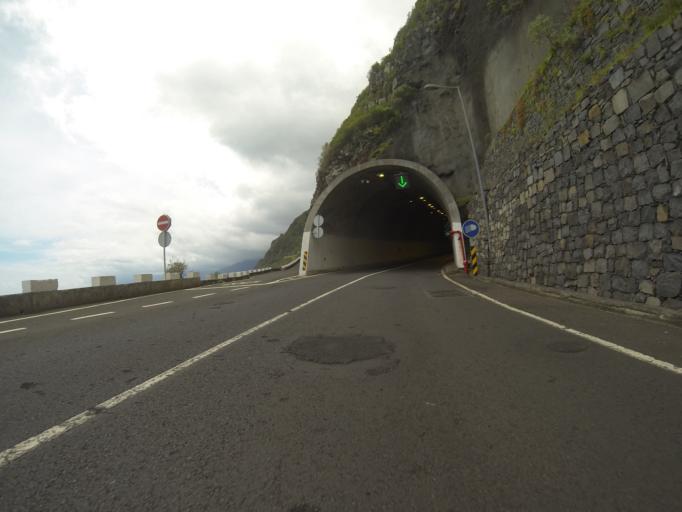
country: PT
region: Madeira
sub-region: Porto Moniz
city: Porto Moniz
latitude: 32.8597
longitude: -17.1631
